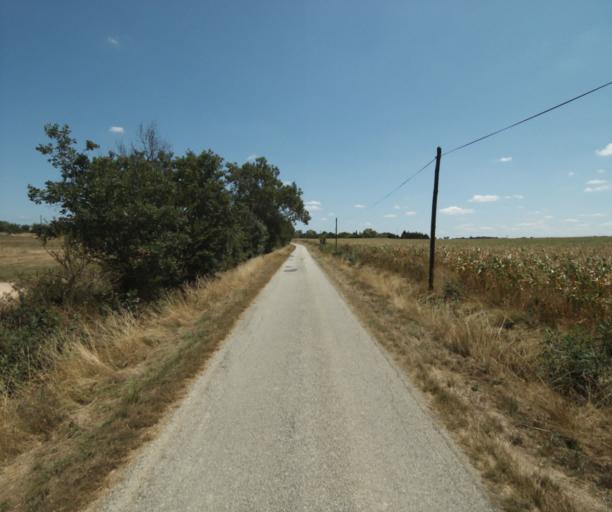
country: FR
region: Midi-Pyrenees
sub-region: Departement de la Haute-Garonne
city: Auriac-sur-Vendinelle
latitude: 43.5005
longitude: 1.8474
